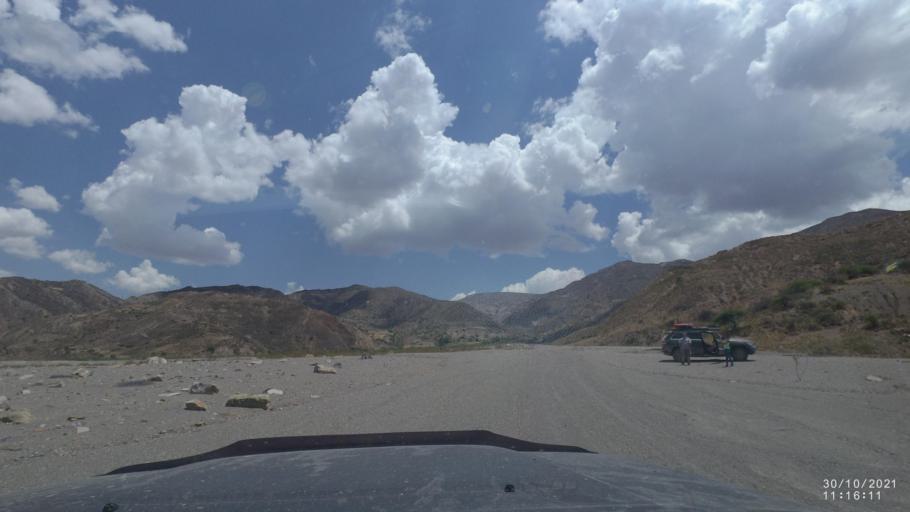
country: BO
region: Cochabamba
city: Sipe Sipe
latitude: -17.5229
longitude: -66.5926
